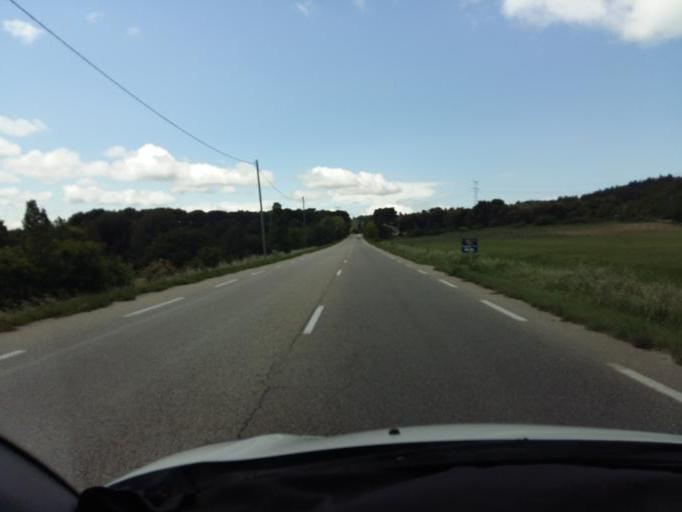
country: FR
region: Provence-Alpes-Cote d'Azur
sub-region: Departement des Bouches-du-Rhone
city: Lambesc
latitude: 43.6743
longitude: 5.2342
